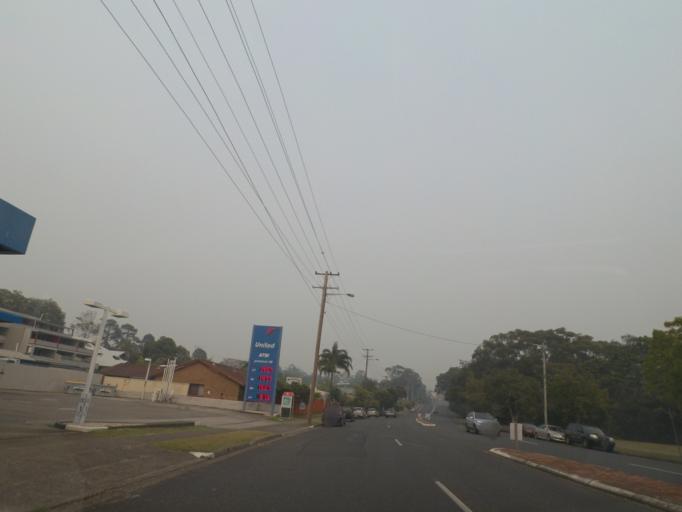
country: AU
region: New South Wales
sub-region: Coffs Harbour
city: Coffs Harbour
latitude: -30.3056
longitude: 153.1322
